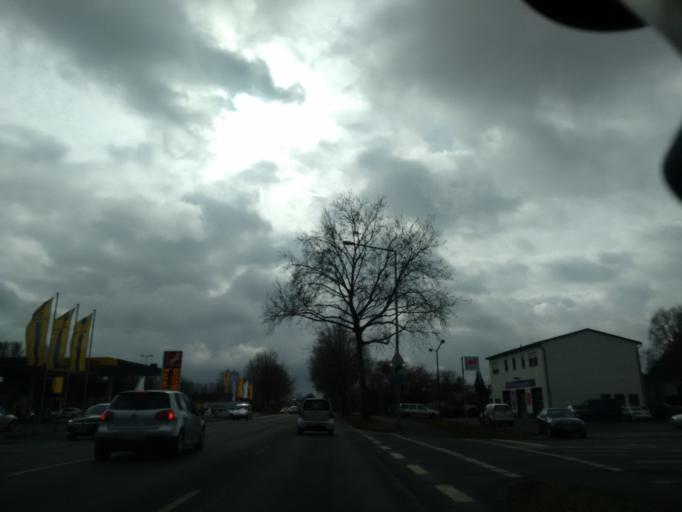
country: DE
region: North Rhine-Westphalia
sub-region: Regierungsbezirk Detmold
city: Paderborn
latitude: 51.7353
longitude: 8.7671
